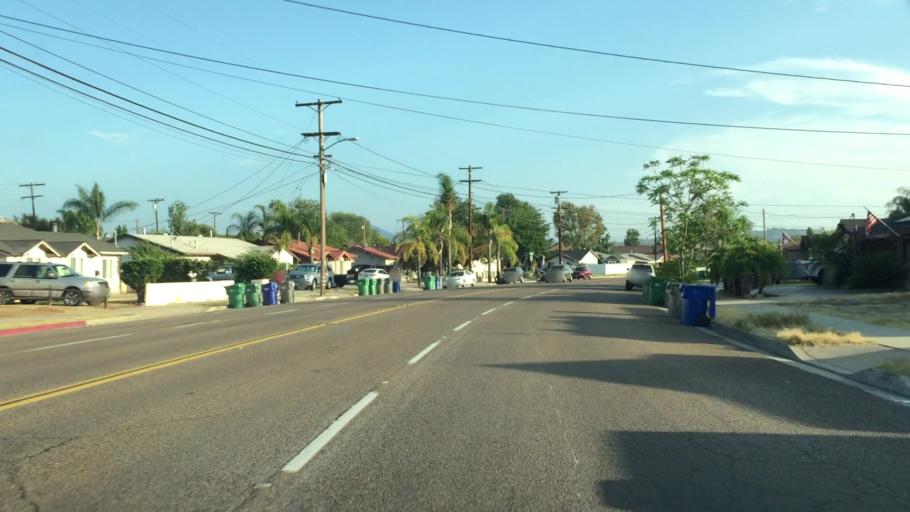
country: US
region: California
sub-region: San Diego County
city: Bostonia
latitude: 32.8154
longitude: -116.9498
